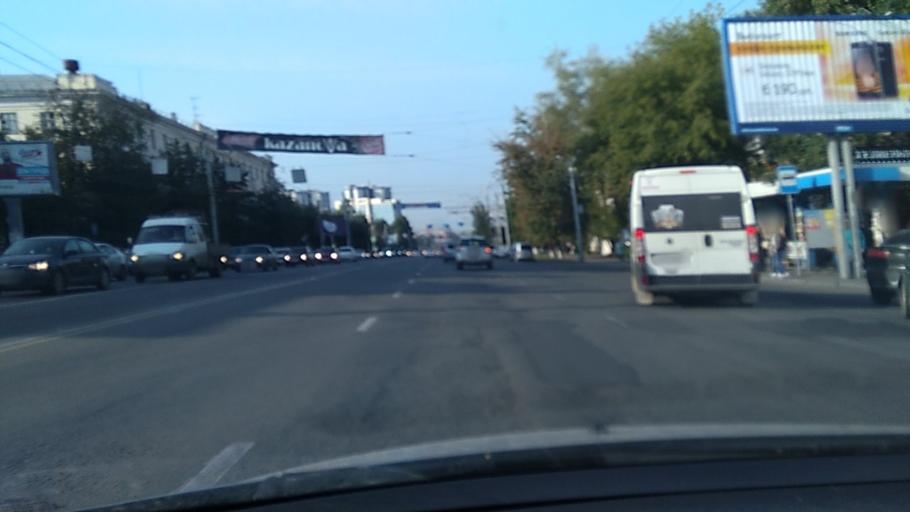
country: RU
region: Chelyabinsk
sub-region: Gorod Chelyabinsk
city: Chelyabinsk
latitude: 55.1603
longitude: 61.3812
